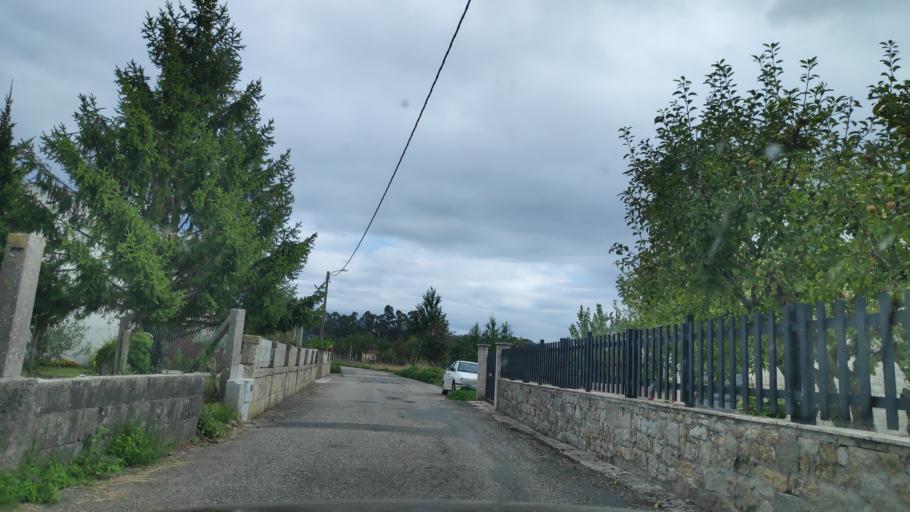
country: ES
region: Galicia
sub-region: Provincia da Coruna
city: Rianxo
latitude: 42.6748
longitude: -8.8144
